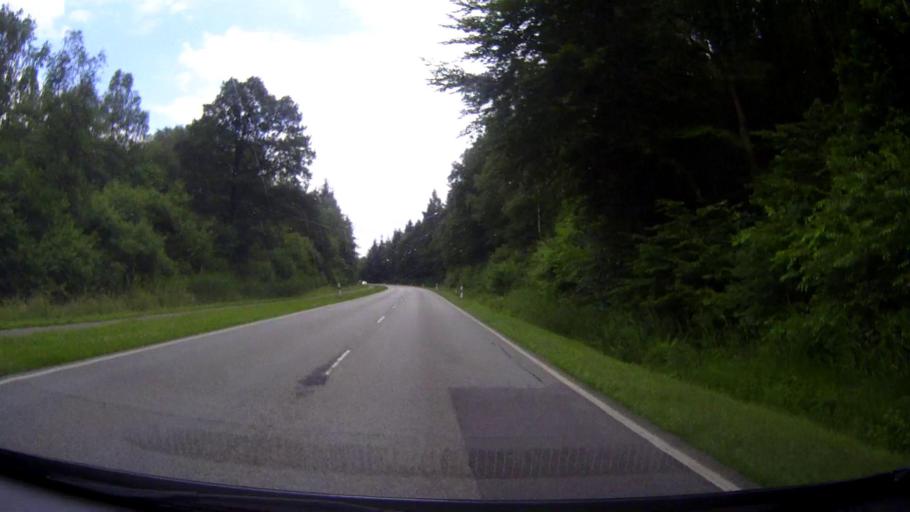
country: DE
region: Schleswig-Holstein
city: Meezen
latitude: 54.0711
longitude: 9.7311
